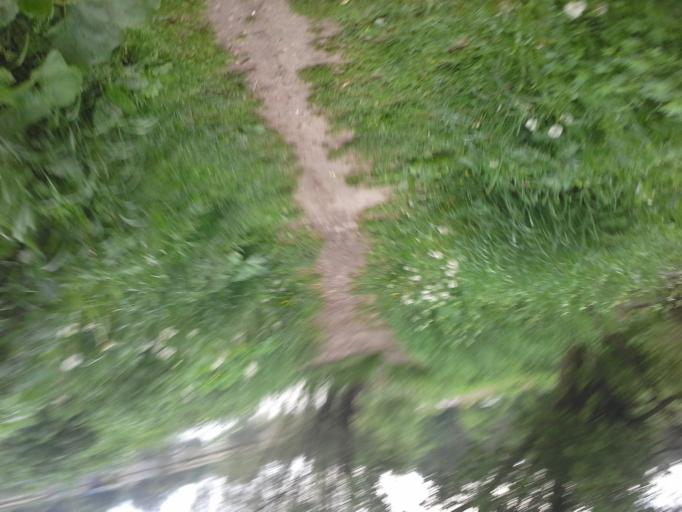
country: RU
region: Moskovskaya
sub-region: Leninskiy Rayon
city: Vnukovo
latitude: 55.6183
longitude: 37.3044
